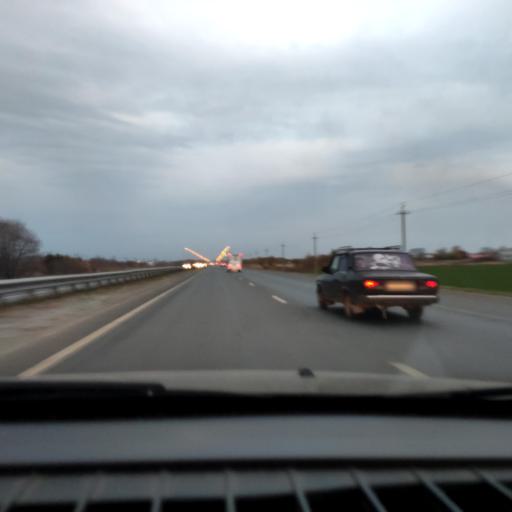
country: RU
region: Samara
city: Tol'yatti
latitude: 53.5758
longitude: 49.4354
